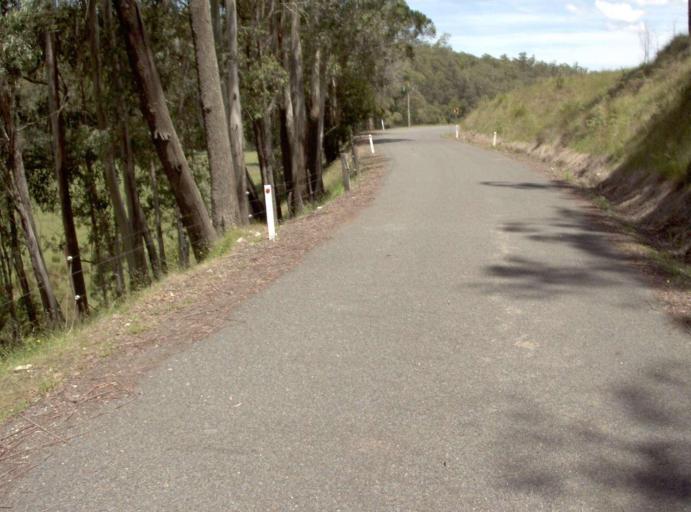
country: AU
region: New South Wales
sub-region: Bombala
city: Bombala
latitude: -37.3690
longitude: 149.0165
